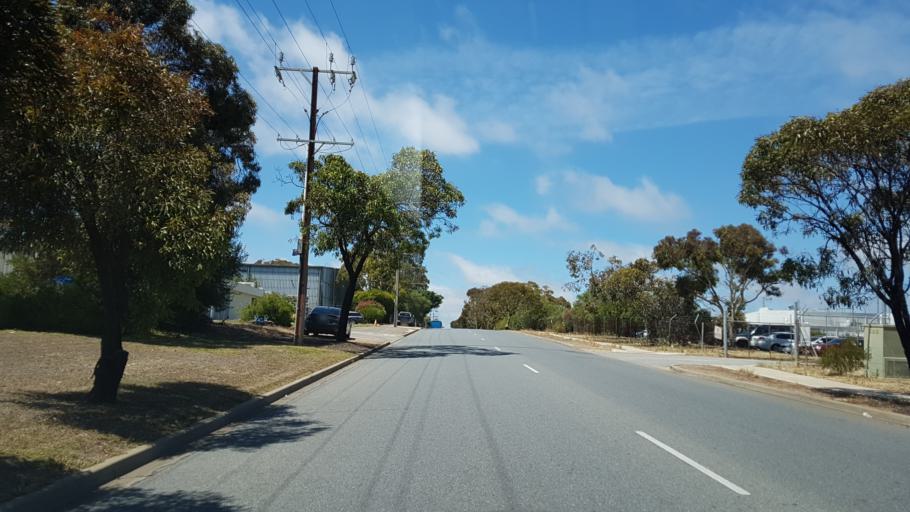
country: AU
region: South Australia
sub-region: Onkaparinga
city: Reynella
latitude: -35.1071
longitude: 138.5069
